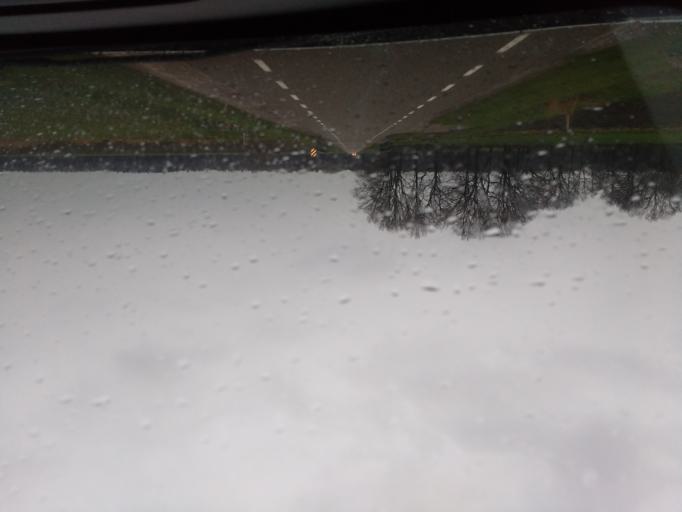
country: NL
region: North Brabant
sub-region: Gemeente Boxmeer
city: Overloon
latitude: 51.5494
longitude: 5.9392
